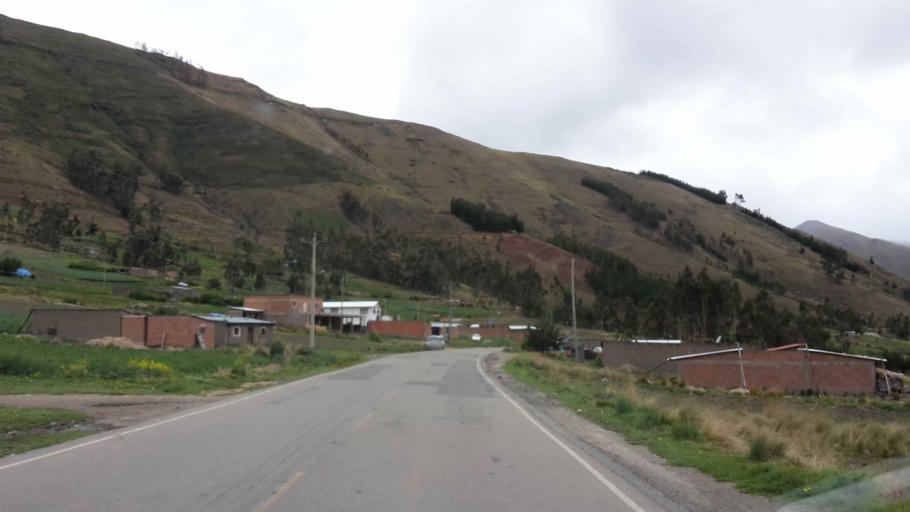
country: BO
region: Cochabamba
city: Arani
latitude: -17.4816
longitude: -65.5458
